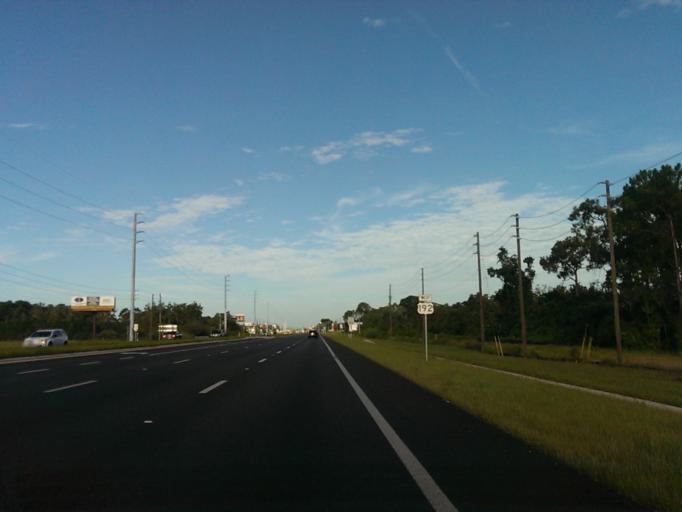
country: US
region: Florida
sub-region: Lake County
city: Four Corners
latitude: 28.3470
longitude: -81.6498
